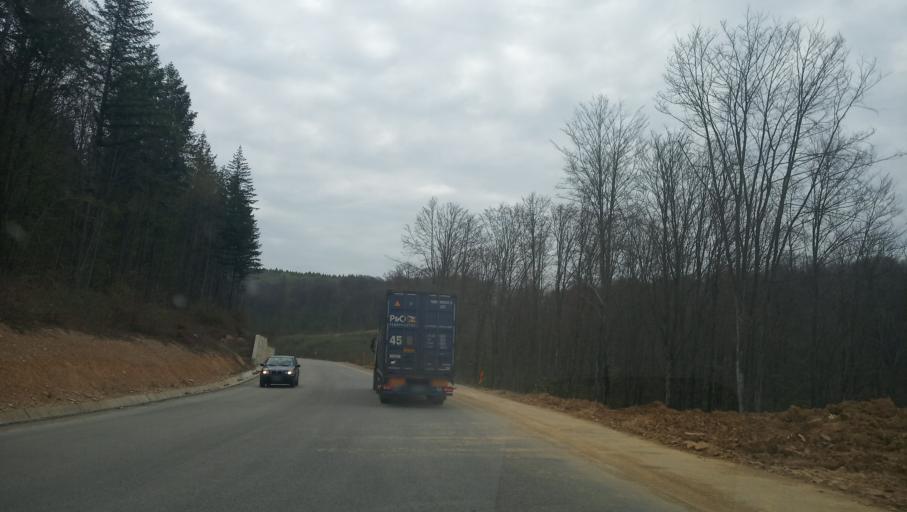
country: RO
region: Bihor
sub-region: Comuna Cristioru de Jos
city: Cristioru de Jos
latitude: 46.4100
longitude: 22.5377
